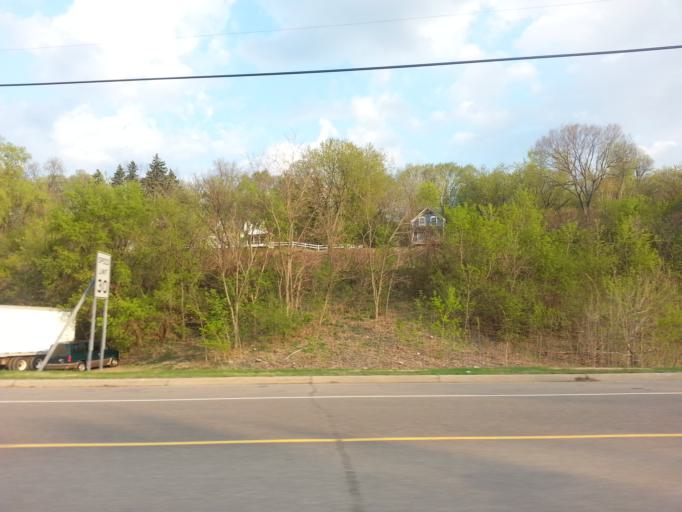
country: US
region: Minnesota
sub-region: Dakota County
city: Mendota Heights
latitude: 44.8870
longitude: -93.1658
